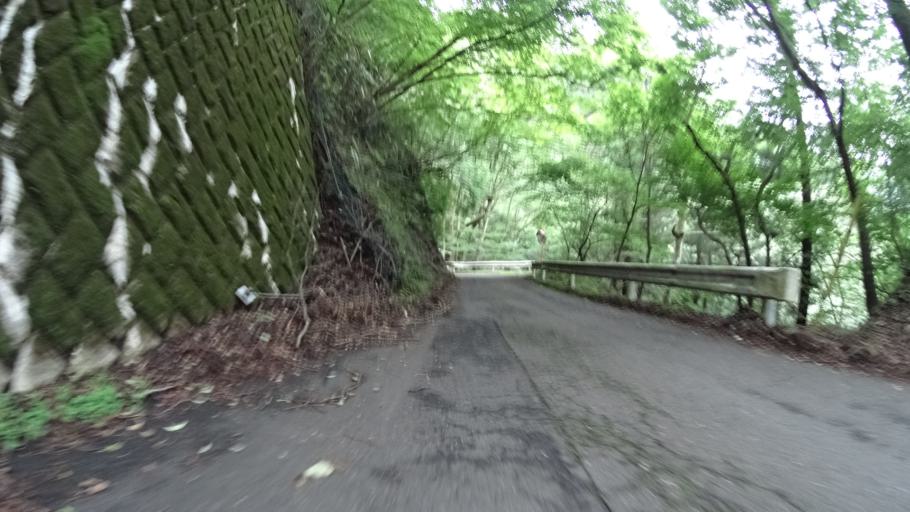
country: JP
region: Kanagawa
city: Hadano
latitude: 35.4726
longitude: 139.2167
